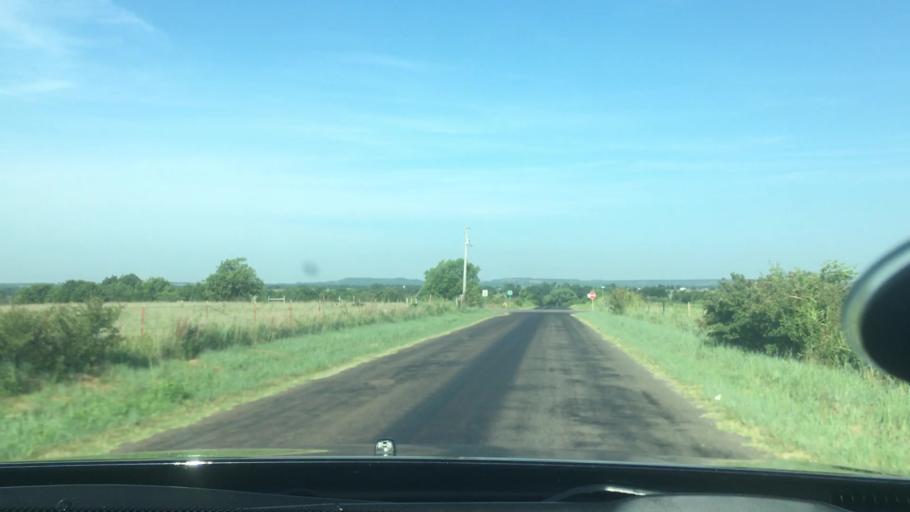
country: US
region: Oklahoma
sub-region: Garvin County
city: Maysville
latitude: 34.6520
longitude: -97.4038
